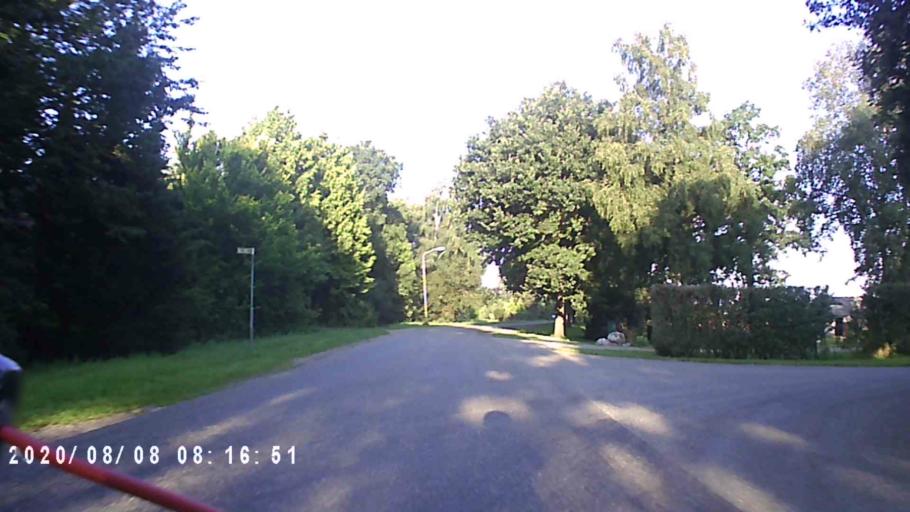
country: NL
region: Groningen
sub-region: Gemeente Leek
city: Leek
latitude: 53.0953
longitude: 6.3333
